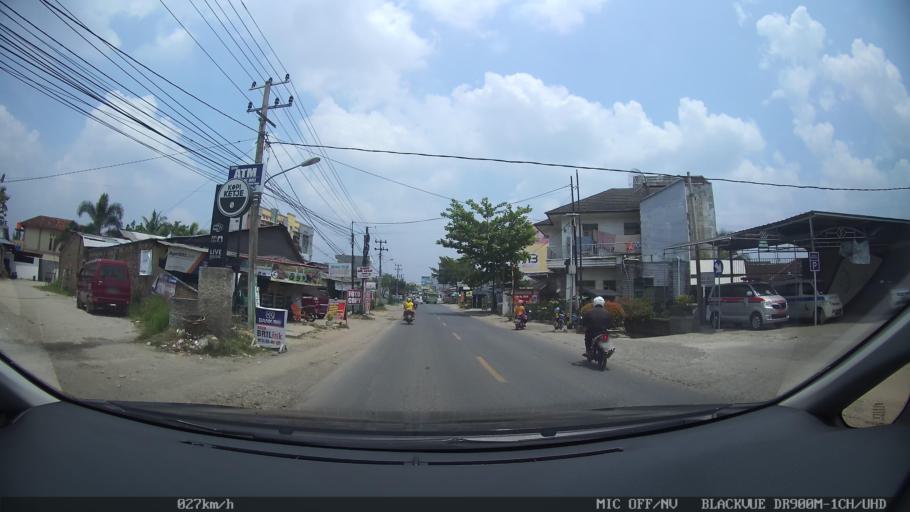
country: ID
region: Lampung
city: Pringsewu
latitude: -5.3587
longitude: 104.9902
